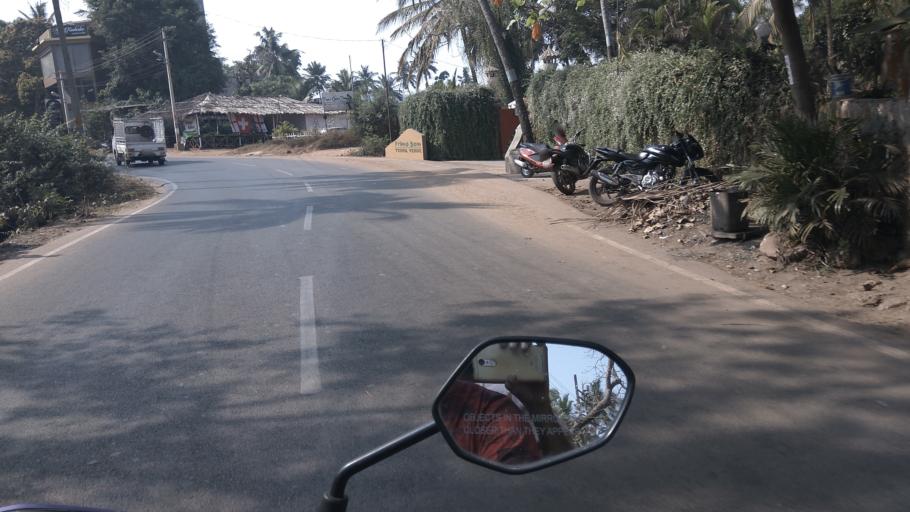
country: IN
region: Goa
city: Calangute
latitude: 15.5566
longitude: 73.7608
